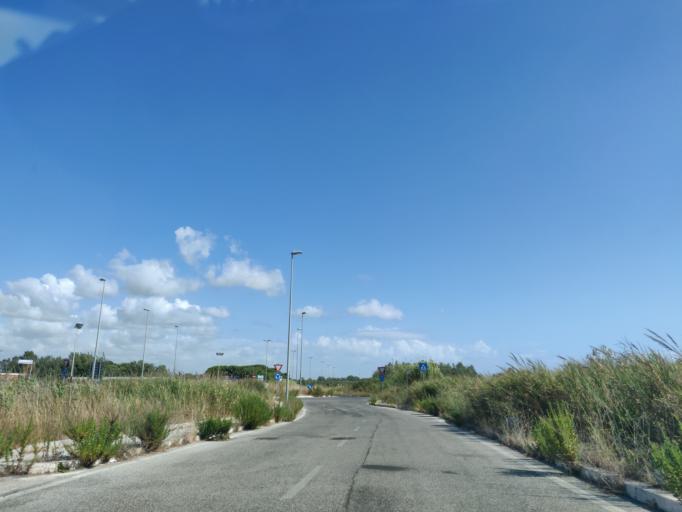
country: IT
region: Latium
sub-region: Citta metropolitana di Roma Capitale
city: Npp 23 (Parco Leonardo)
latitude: 41.7953
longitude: 12.2899
